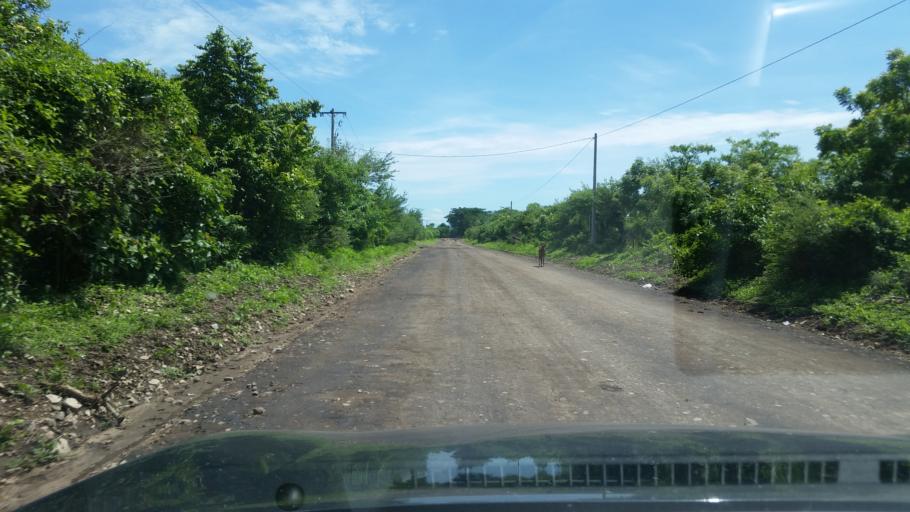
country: NI
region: Chinandega
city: El Viejo
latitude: 12.7507
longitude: -87.1338
